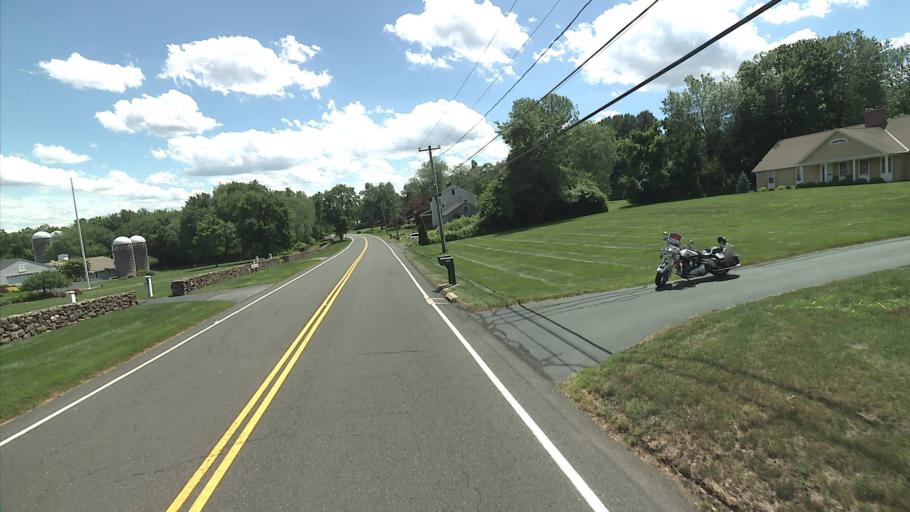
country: US
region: Connecticut
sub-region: Tolland County
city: Somers
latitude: 42.0201
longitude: -72.4846
